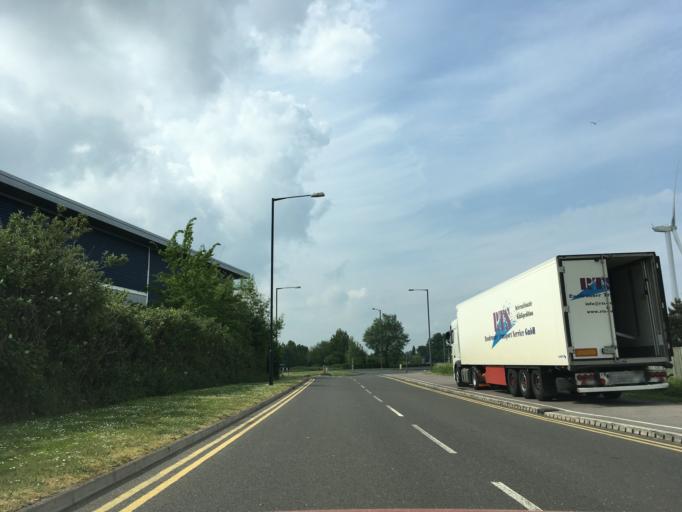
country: GB
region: England
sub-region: South Gloucestershire
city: Severn Beach
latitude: 51.5168
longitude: -2.6671
